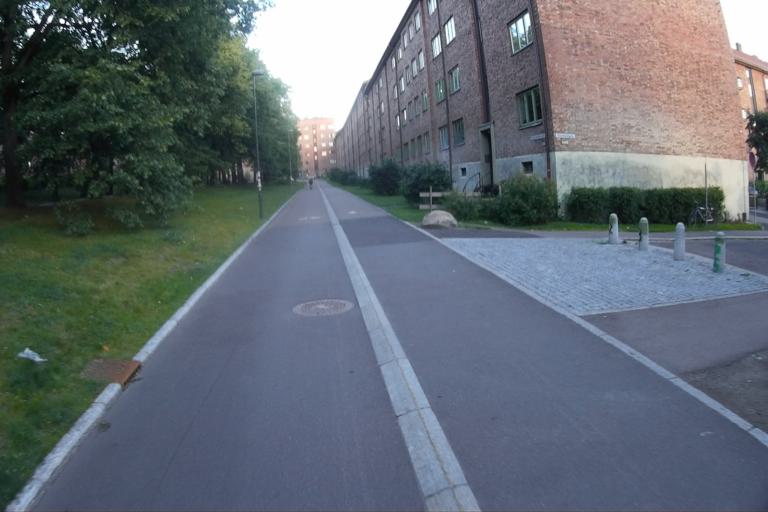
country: NO
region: Oslo
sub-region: Oslo
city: Oslo
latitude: 59.9283
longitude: 10.7711
